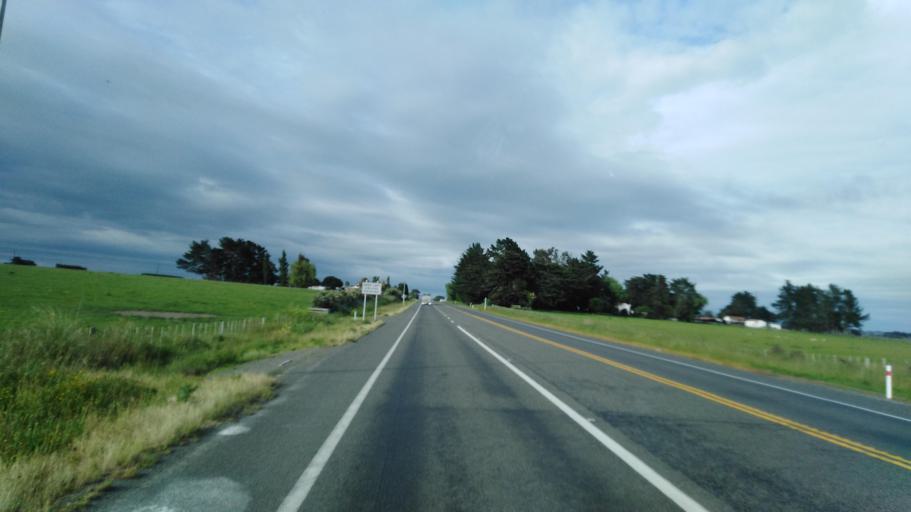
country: NZ
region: Manawatu-Wanganui
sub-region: Rangitikei District
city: Bulls
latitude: -40.2297
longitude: 175.4152
